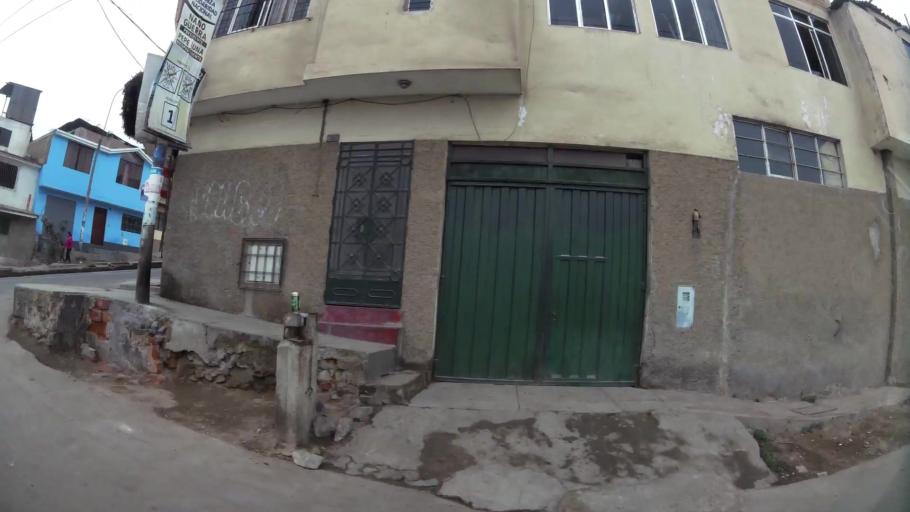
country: PE
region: Lima
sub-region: Lima
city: Surco
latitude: -12.1788
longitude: -76.9598
